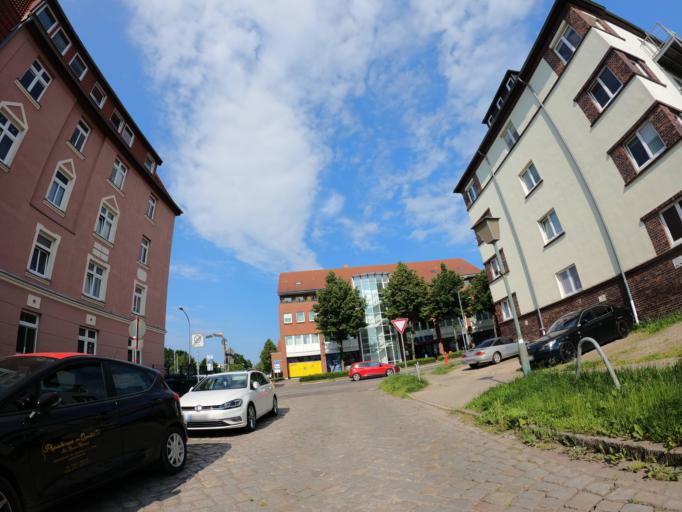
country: DE
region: Mecklenburg-Vorpommern
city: Stralsund
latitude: 54.3052
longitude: 13.0704
